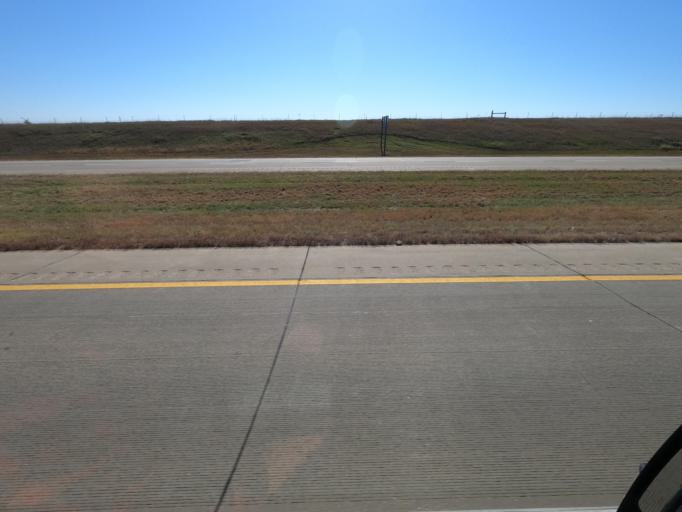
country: US
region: Kansas
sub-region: Dickinson County
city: Chapman
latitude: 38.9630
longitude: -97.1004
